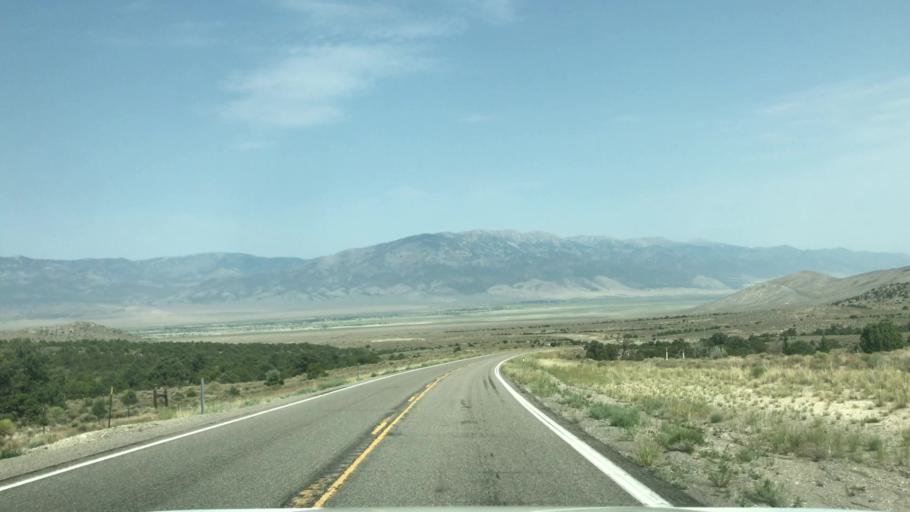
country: US
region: Nevada
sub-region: White Pine County
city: McGill
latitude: 39.1656
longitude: -114.3633
